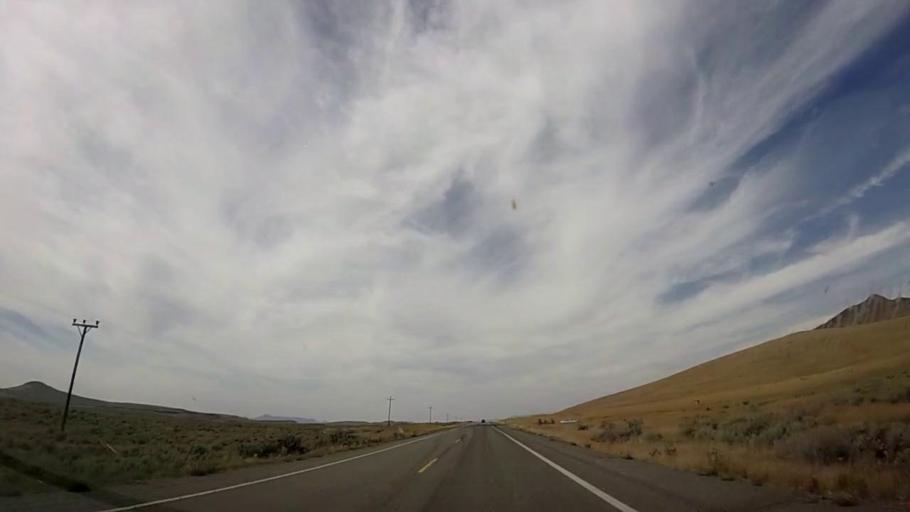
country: US
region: Idaho
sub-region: Blaine County
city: Bellevue
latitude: 43.2331
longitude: -114.3123
